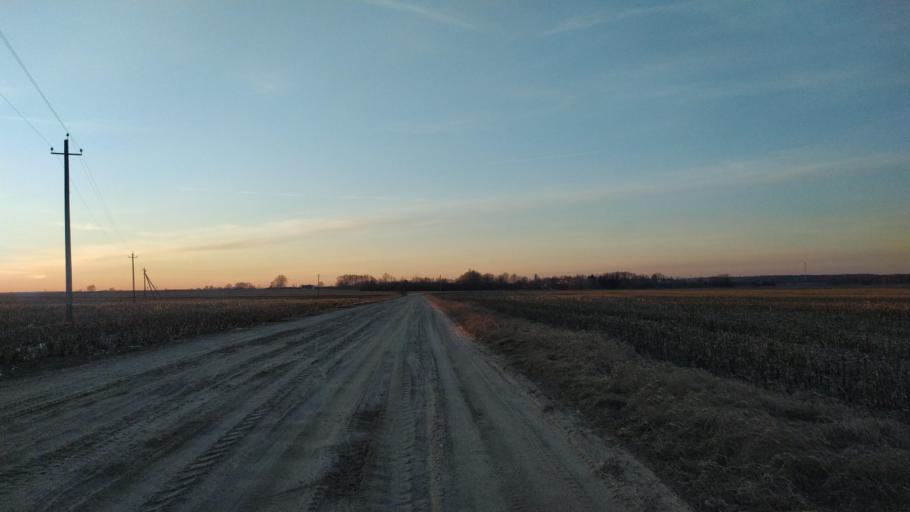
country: BY
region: Brest
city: Pruzhany
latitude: 52.5479
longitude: 24.2384
